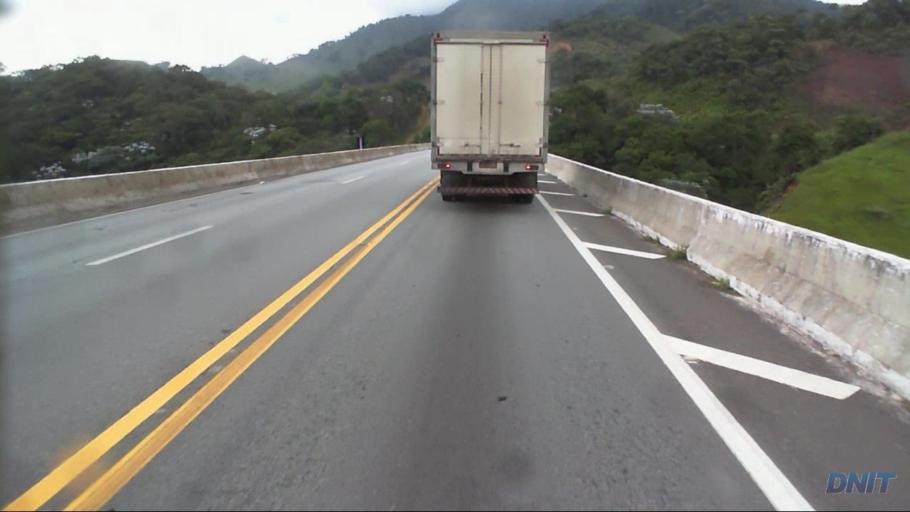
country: BR
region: Minas Gerais
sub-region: Nova Era
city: Nova Era
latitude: -19.6551
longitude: -42.9559
